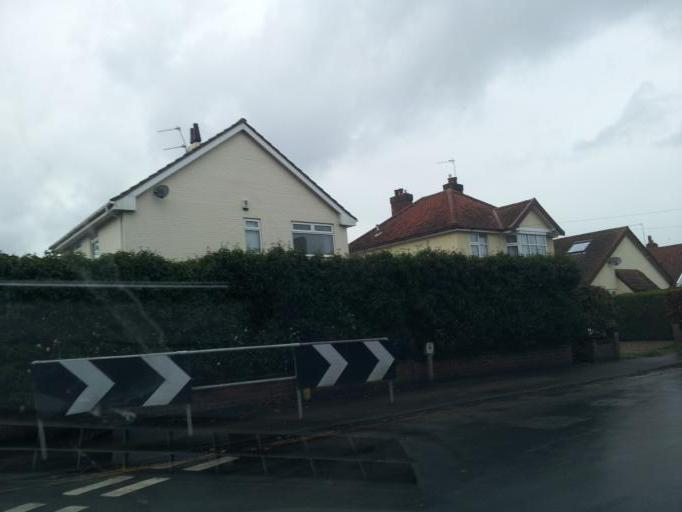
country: GB
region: England
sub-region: Norfolk
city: Brundall
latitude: 52.6254
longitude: 1.4257
